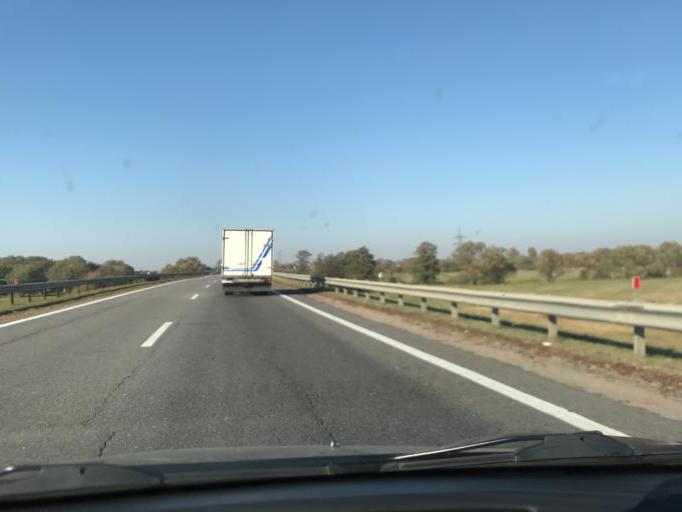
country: BY
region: Minsk
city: Dukora
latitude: 53.6623
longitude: 27.9435
